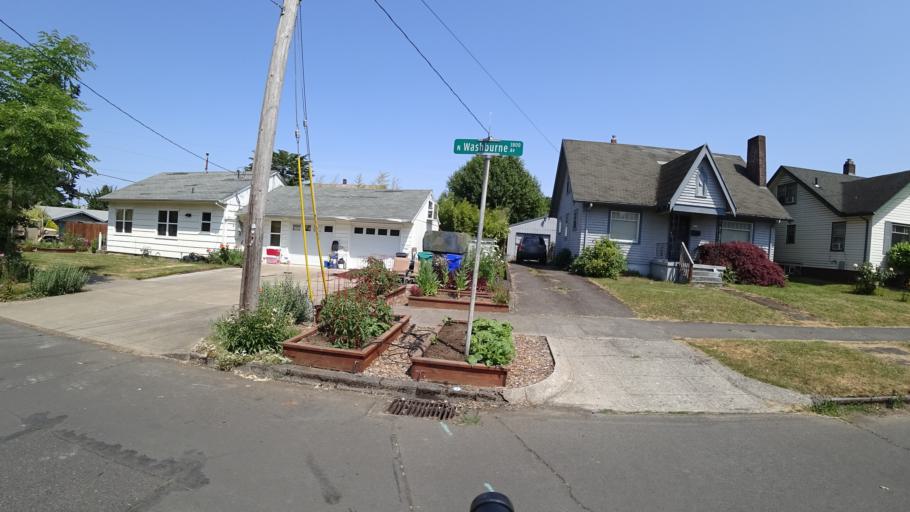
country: US
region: Oregon
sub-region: Multnomah County
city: Portland
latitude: 45.5823
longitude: -122.7053
